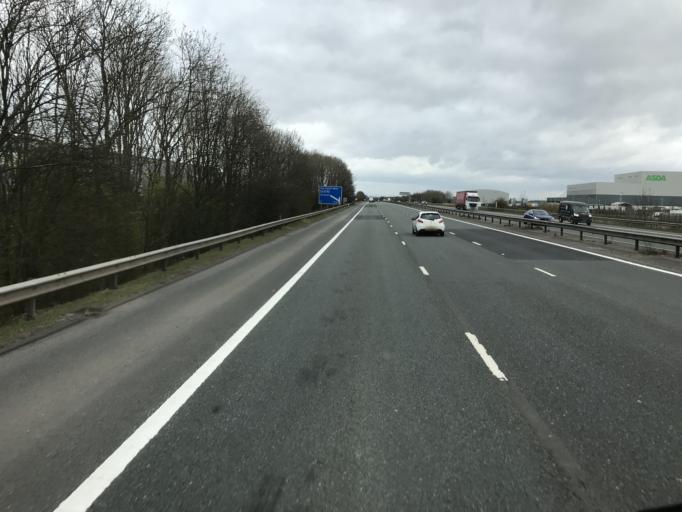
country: GB
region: England
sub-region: Warrington
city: Burtonwood
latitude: 53.4138
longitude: -2.6687
